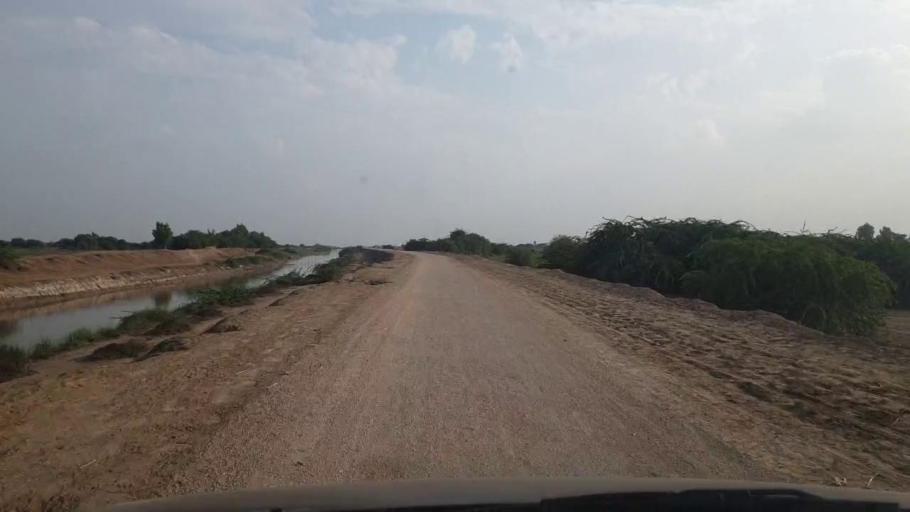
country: PK
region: Sindh
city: Badin
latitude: 24.5482
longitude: 68.6713
